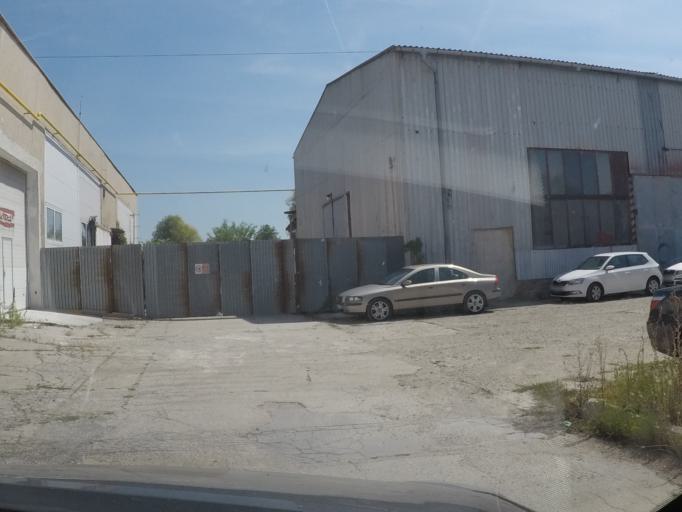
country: SK
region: Nitriansky
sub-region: Okres Nitra
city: Nitra
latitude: 48.2884
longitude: 18.0917
